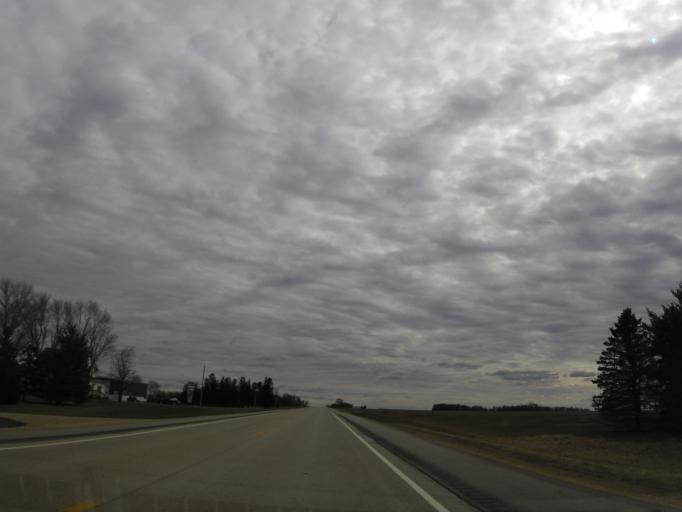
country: US
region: Minnesota
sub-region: Fillmore County
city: Spring Valley
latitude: 43.5238
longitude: -92.3694
